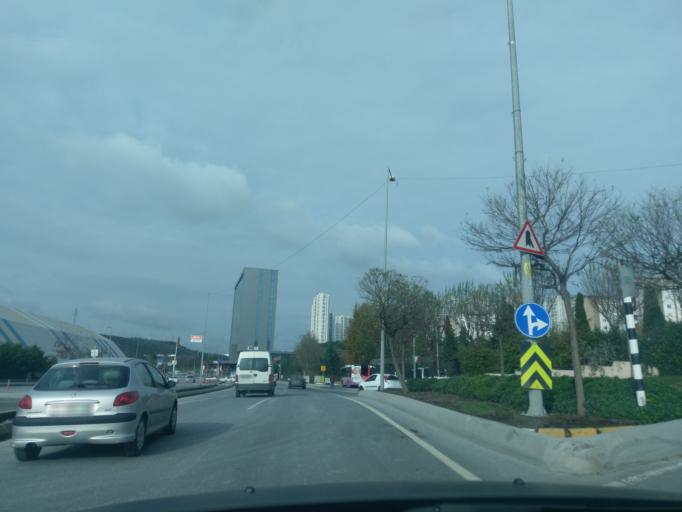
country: TR
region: Istanbul
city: Basaksehir
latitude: 41.0568
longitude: 28.7748
